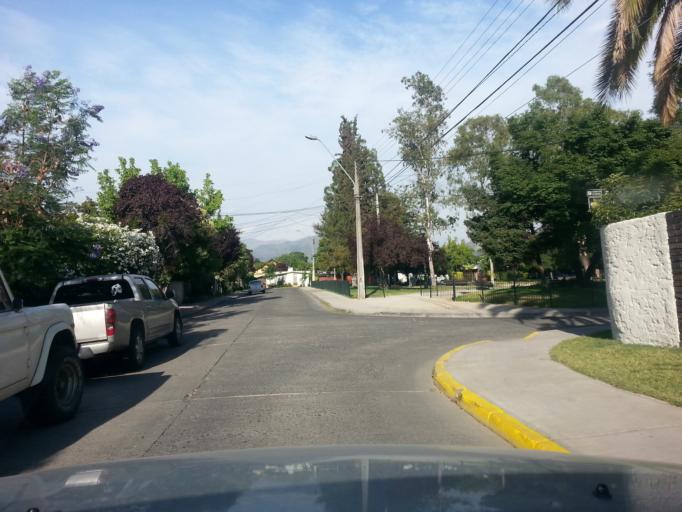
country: CL
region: Santiago Metropolitan
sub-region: Provincia de Santiago
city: Villa Presidente Frei, Nunoa, Santiago, Chile
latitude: -33.3864
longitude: -70.5485
